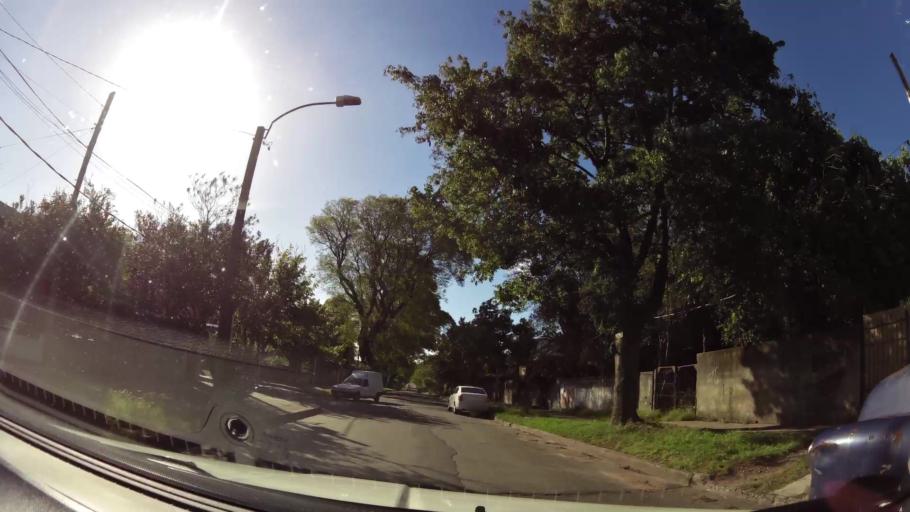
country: UY
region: Montevideo
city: Montevideo
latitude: -34.8506
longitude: -56.2134
